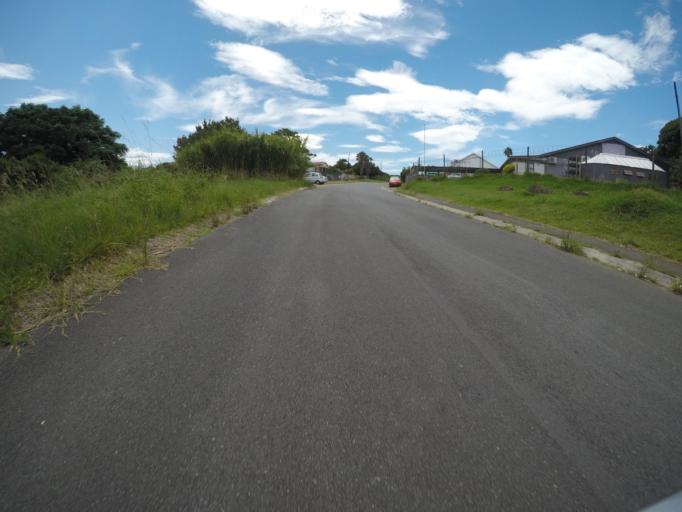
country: ZA
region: Eastern Cape
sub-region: Buffalo City Metropolitan Municipality
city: East London
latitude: -33.0417
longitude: 27.8539
